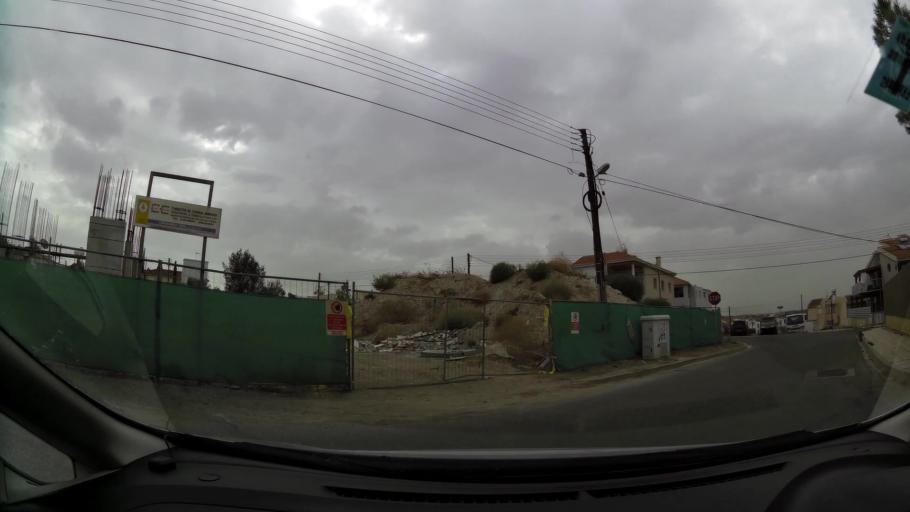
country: CY
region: Lefkosia
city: Geri
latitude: 35.0992
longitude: 33.3782
